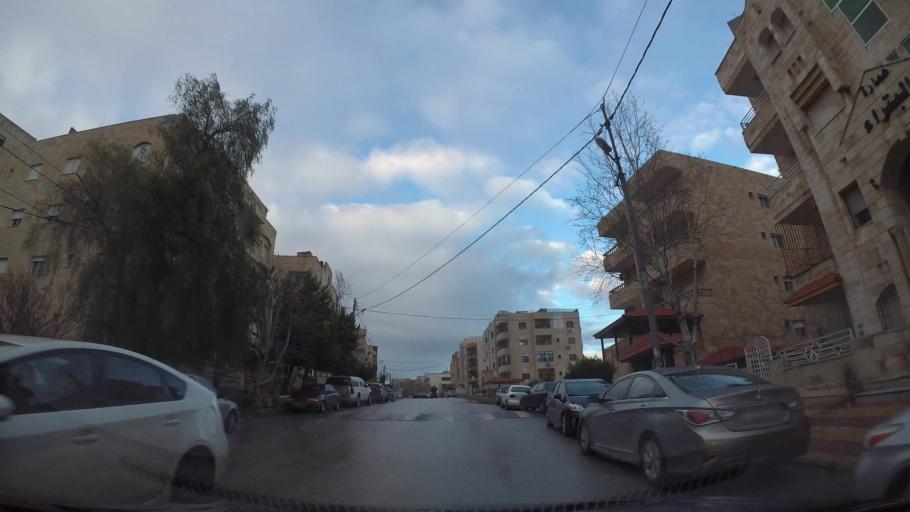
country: JO
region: Amman
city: Amman
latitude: 31.9796
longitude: 35.9143
